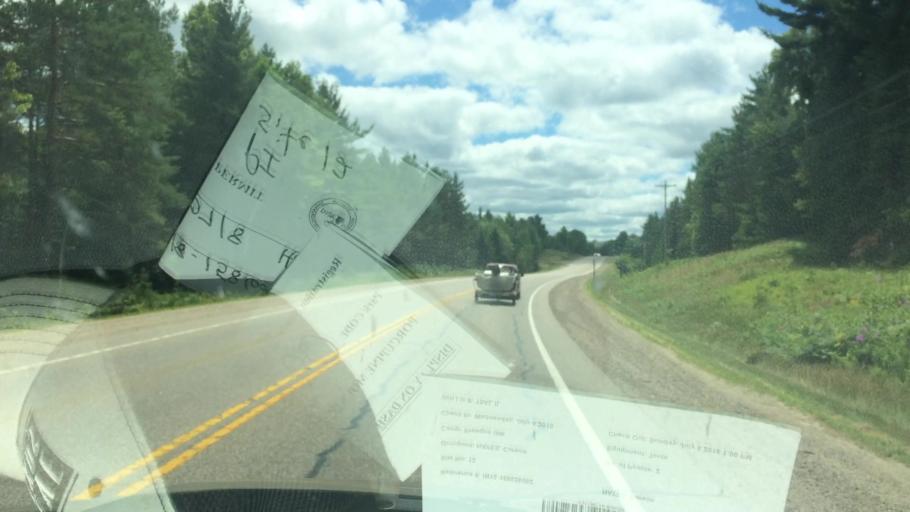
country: US
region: Wisconsin
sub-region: Vilas County
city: Eagle River
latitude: 45.7989
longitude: -89.3201
